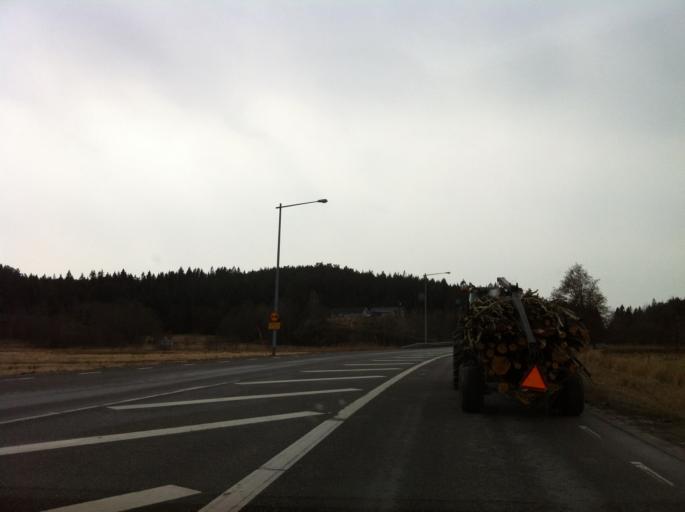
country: SE
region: Vaestra Goetaland
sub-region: Orust
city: Henan
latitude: 58.3157
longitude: 11.6862
